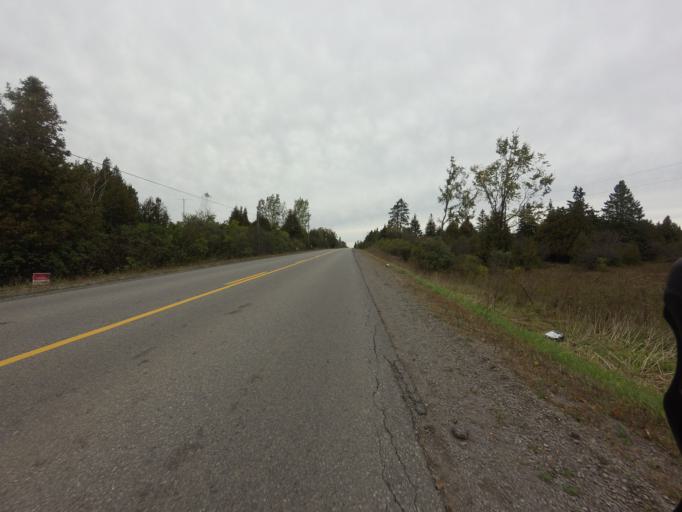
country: CA
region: Ontario
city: Brockville
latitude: 44.7892
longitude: -75.7751
